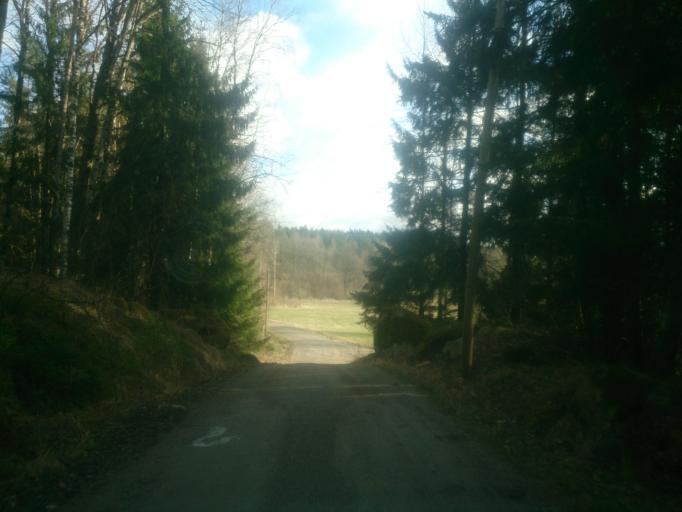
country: SE
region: OEstergoetland
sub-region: Atvidabergs Kommun
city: Atvidaberg
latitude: 58.2359
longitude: 16.1788
